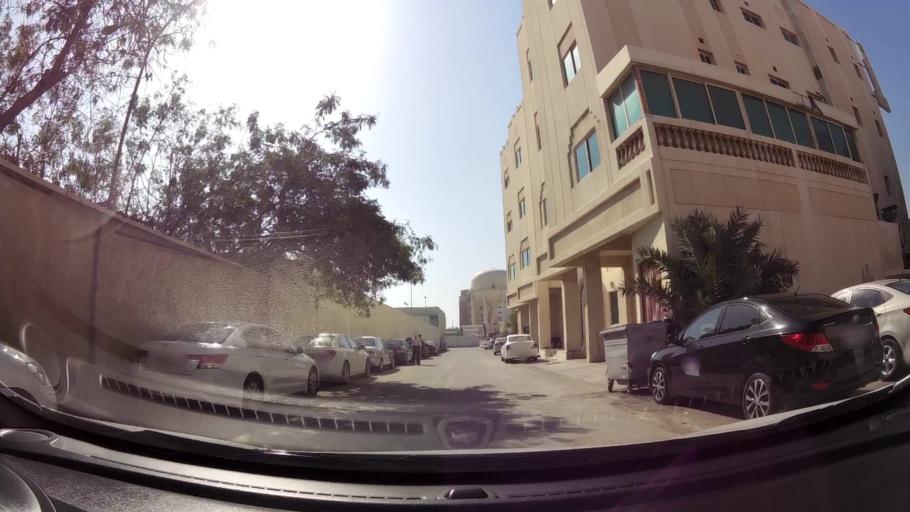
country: BH
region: Manama
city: Manama
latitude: 26.2075
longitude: 50.5924
